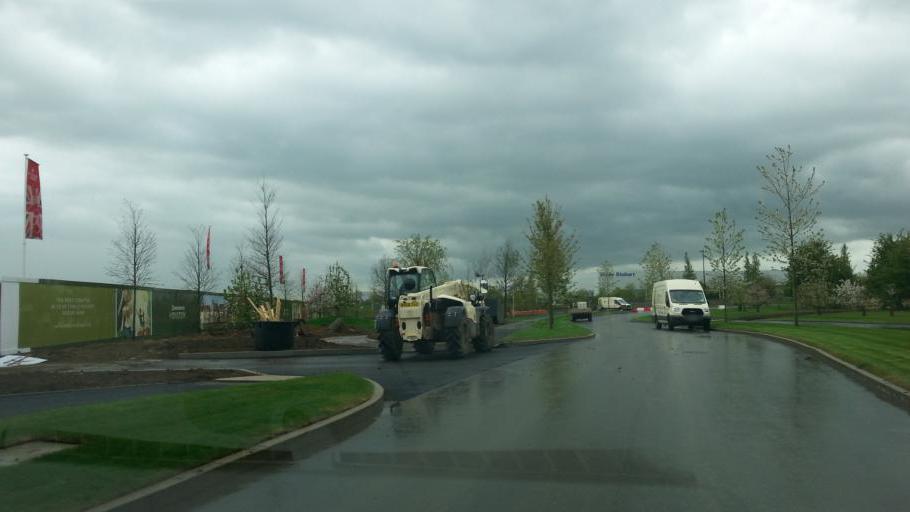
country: GB
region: England
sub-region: Warwickshire
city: Rugby
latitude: 52.3572
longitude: -1.1880
